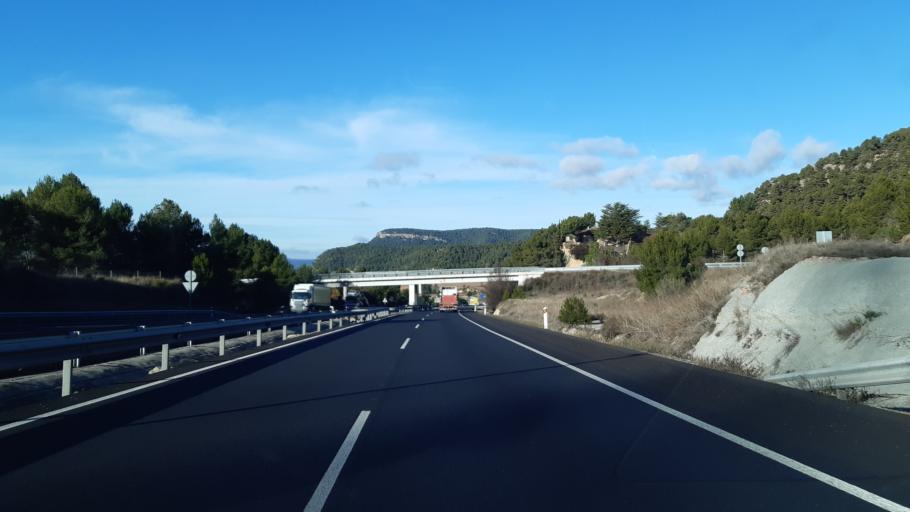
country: ES
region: Catalonia
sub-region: Provincia de Barcelona
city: Castelloli
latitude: 41.5976
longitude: 1.7130
